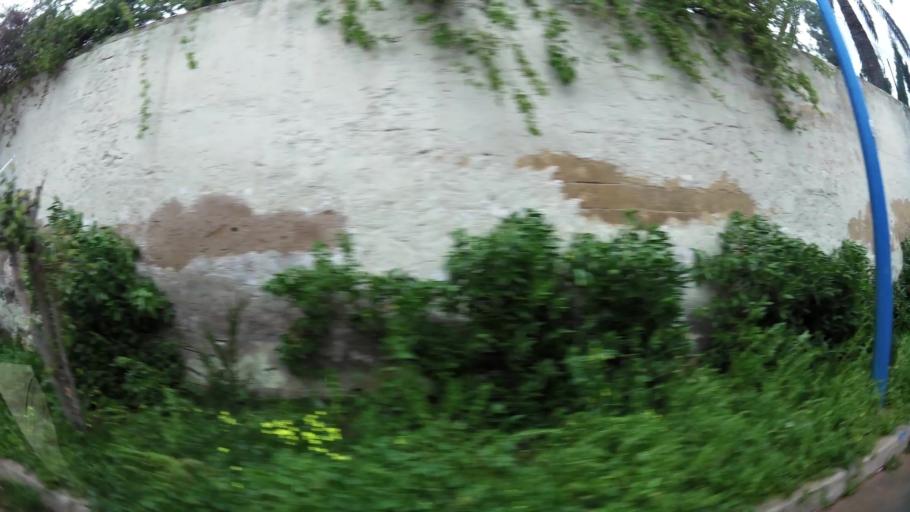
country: MA
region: Grand Casablanca
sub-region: Casablanca
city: Casablanca
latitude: 33.5439
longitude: -7.6361
